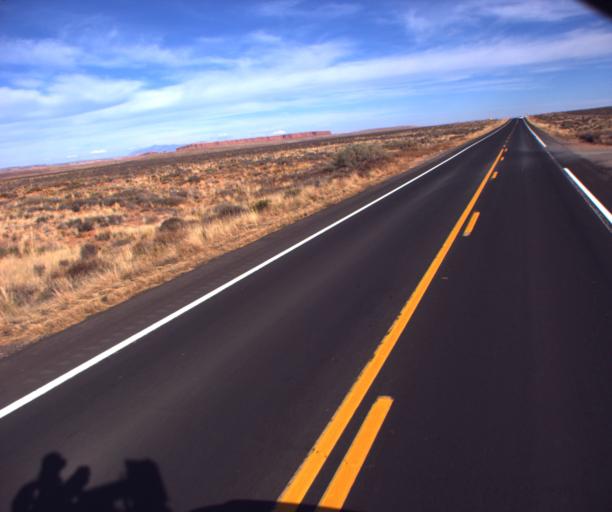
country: US
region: Arizona
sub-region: Apache County
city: Lukachukai
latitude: 36.9633
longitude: -109.4564
